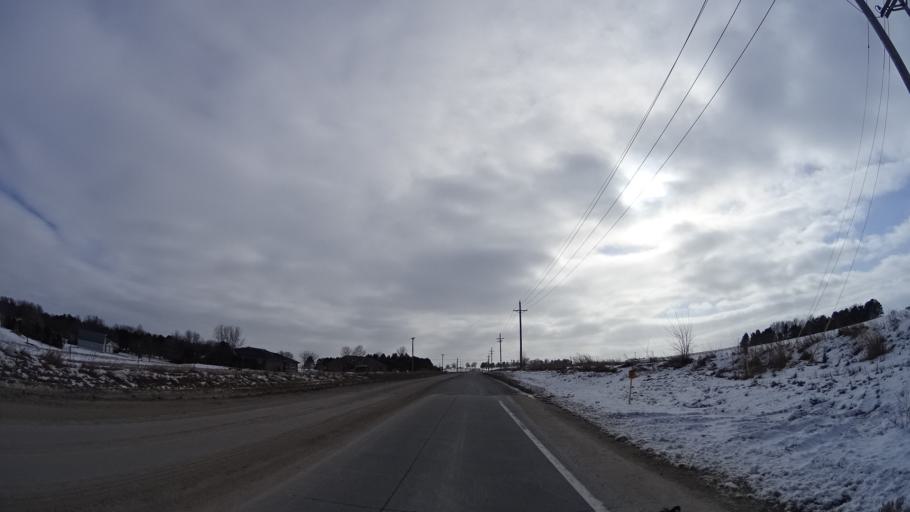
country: US
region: Nebraska
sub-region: Sarpy County
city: Papillion
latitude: 41.1212
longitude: -96.0237
